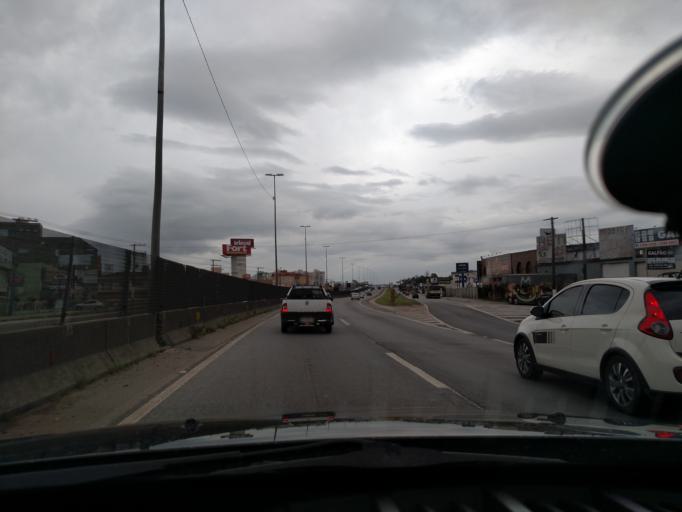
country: BR
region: Santa Catarina
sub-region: Sao Jose
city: Campinas
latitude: -27.5566
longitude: -48.6191
